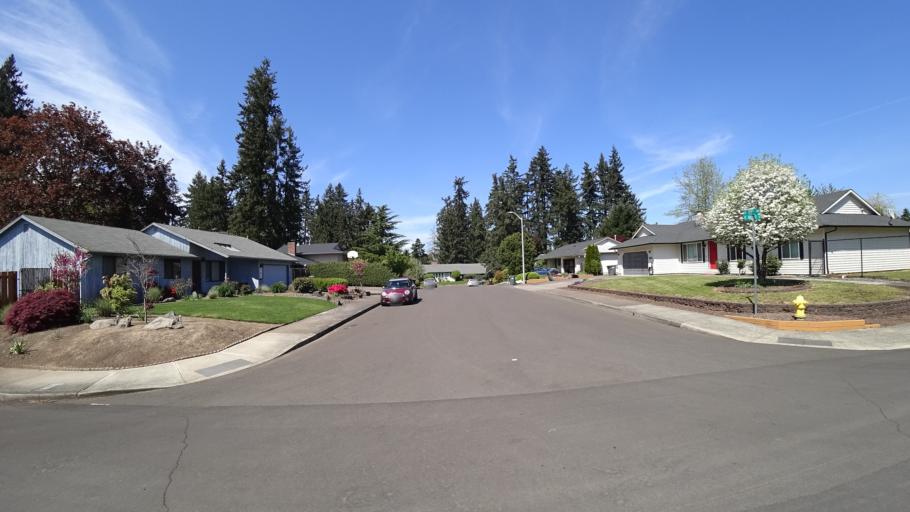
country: US
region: Oregon
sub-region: Washington County
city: Hillsboro
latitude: 45.5170
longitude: -122.9525
